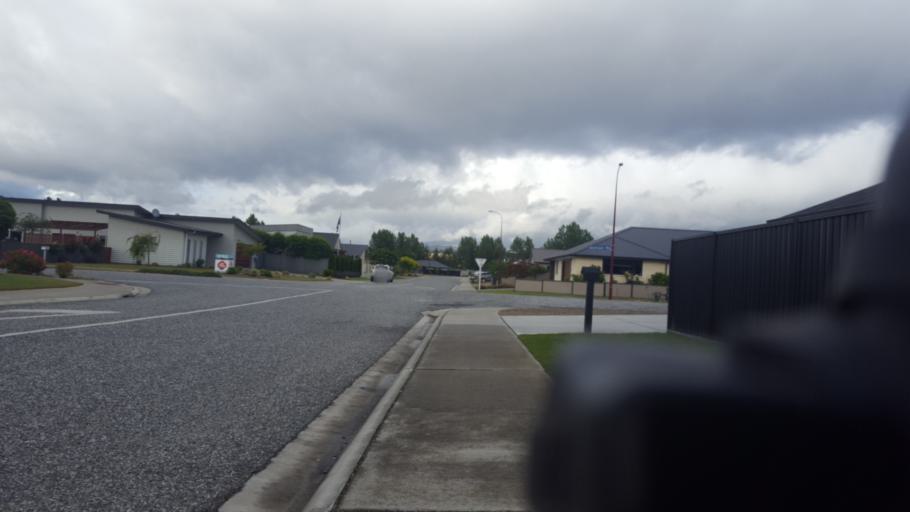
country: NZ
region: Otago
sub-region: Queenstown-Lakes District
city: Wanaka
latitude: -45.2394
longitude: 169.3790
